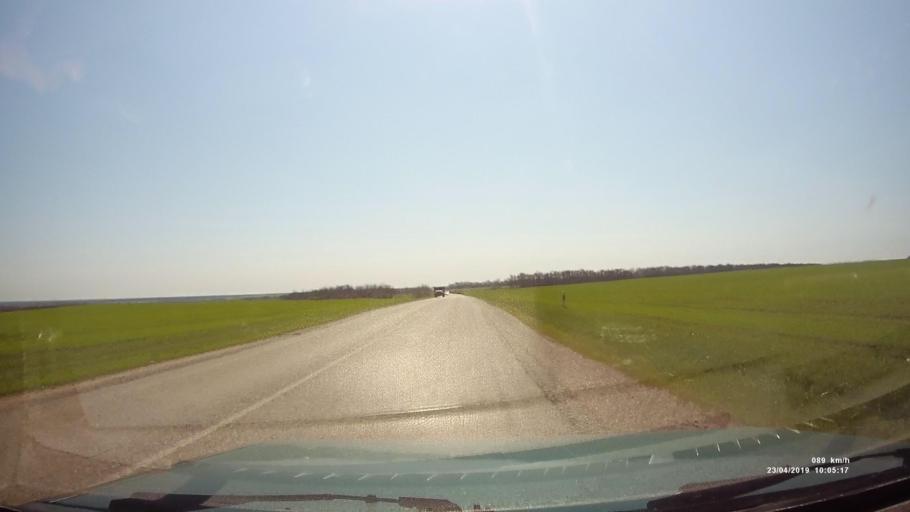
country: RU
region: Rostov
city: Sovetskoye
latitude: 46.7423
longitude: 42.2175
